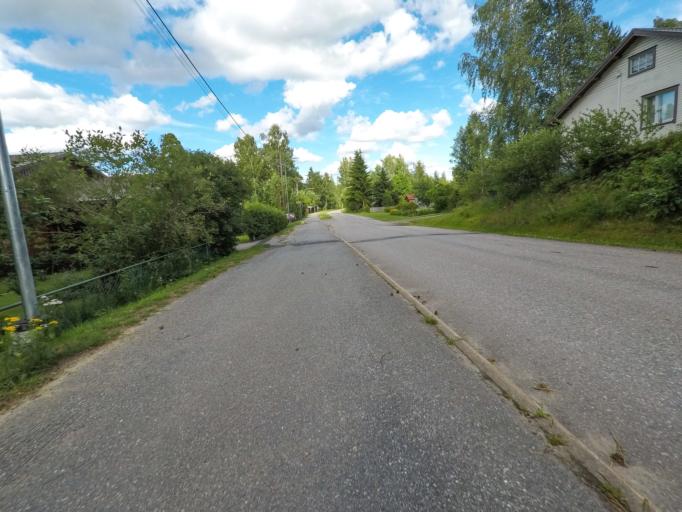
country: FI
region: South Karelia
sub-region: Lappeenranta
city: Joutseno
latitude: 61.1227
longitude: 28.4804
